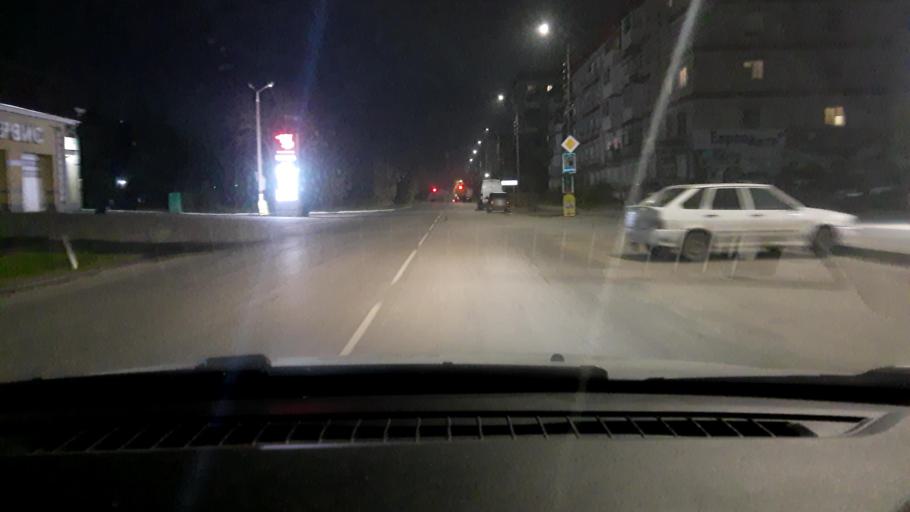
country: RU
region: Nizjnij Novgorod
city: Dzerzhinsk
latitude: 56.2559
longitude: 43.4623
